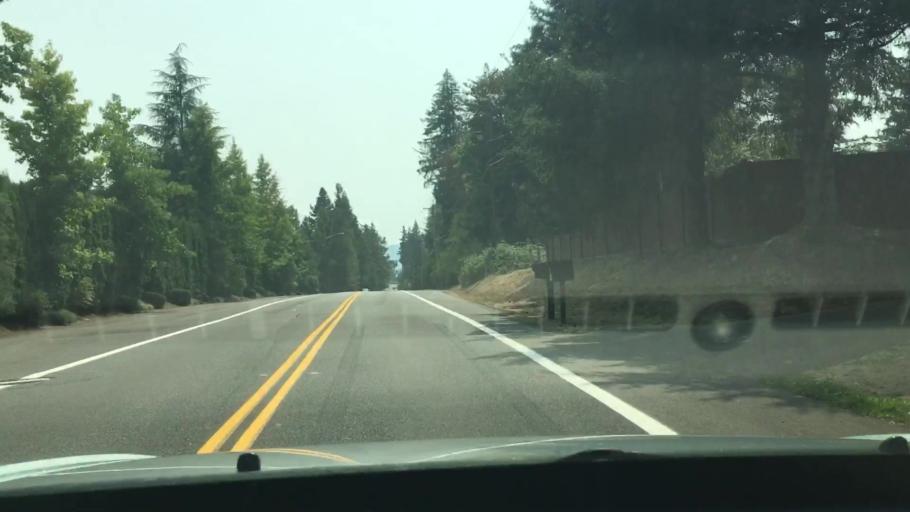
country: US
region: Washington
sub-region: King County
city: City of Sammamish
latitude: 47.5888
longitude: -122.0568
